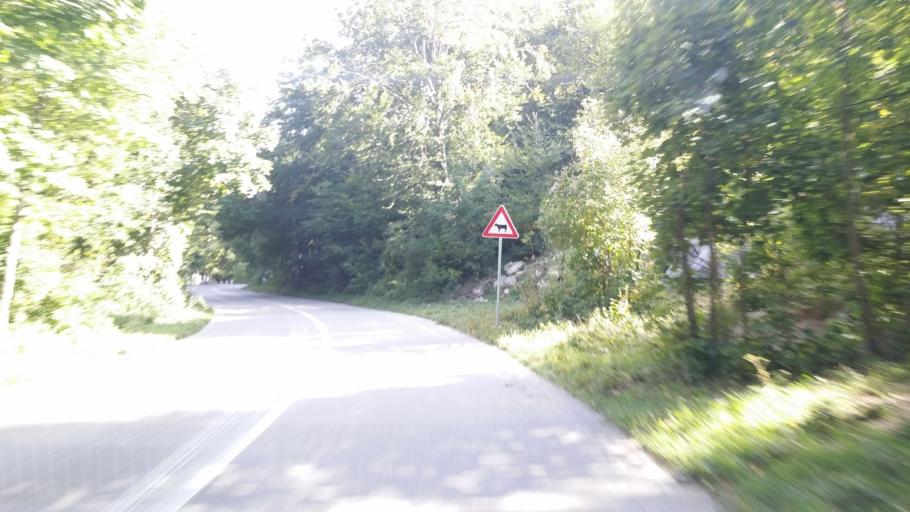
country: HR
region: Primorsko-Goranska
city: Novi Vinodolski
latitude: 45.1797
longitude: 14.8746
